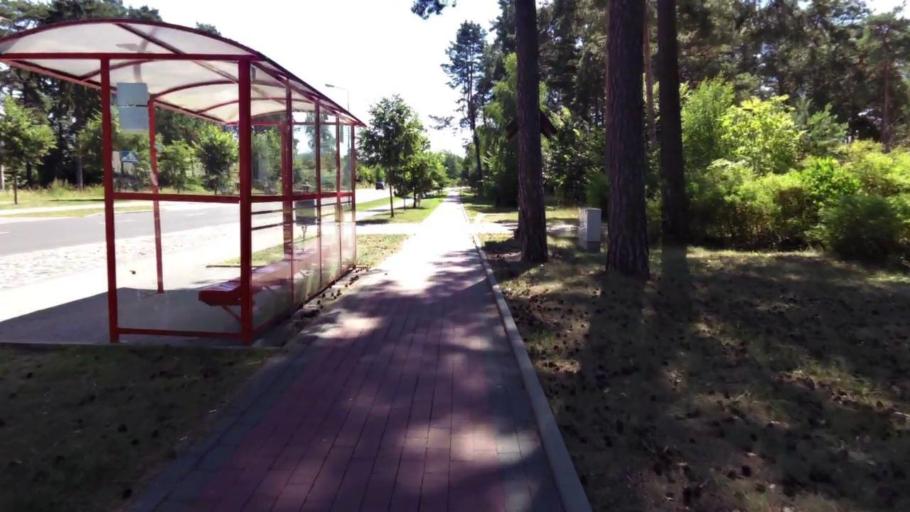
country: PL
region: West Pomeranian Voivodeship
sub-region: Powiat szczecinecki
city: Borne Sulinowo
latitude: 53.5806
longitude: 16.5473
